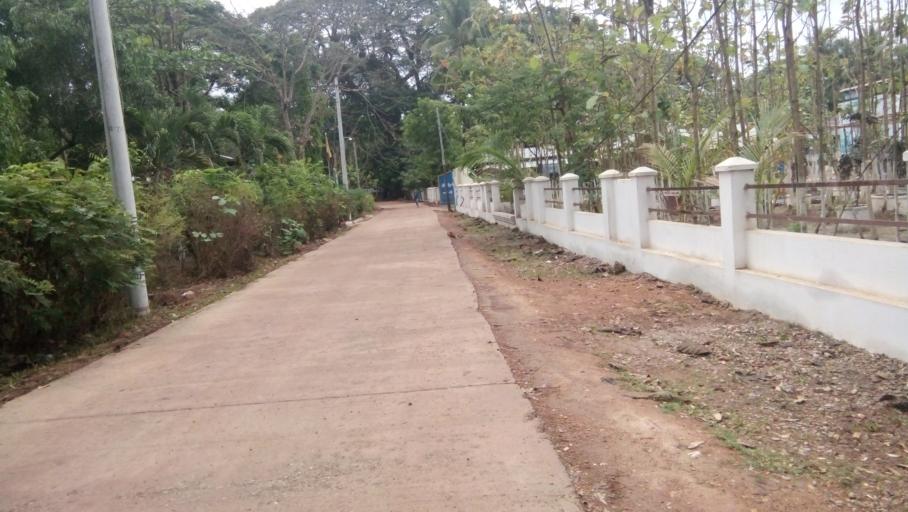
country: MM
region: Kayin
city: Hpa-an
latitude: 17.1195
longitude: 97.8174
